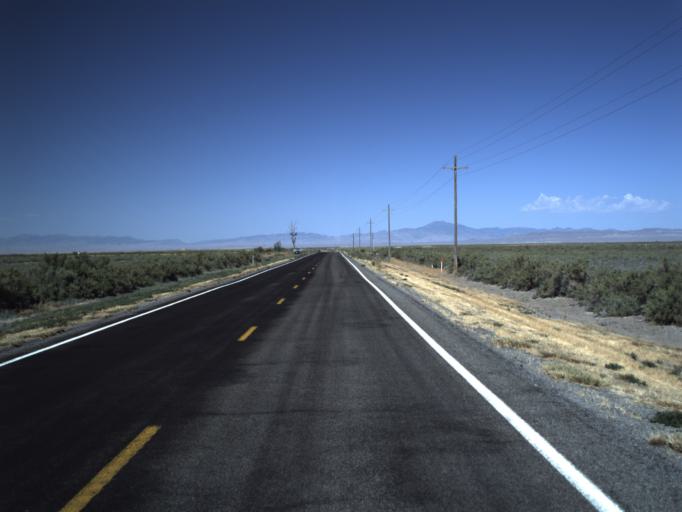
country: US
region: Utah
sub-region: Millard County
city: Delta
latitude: 39.3309
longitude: -112.7016
